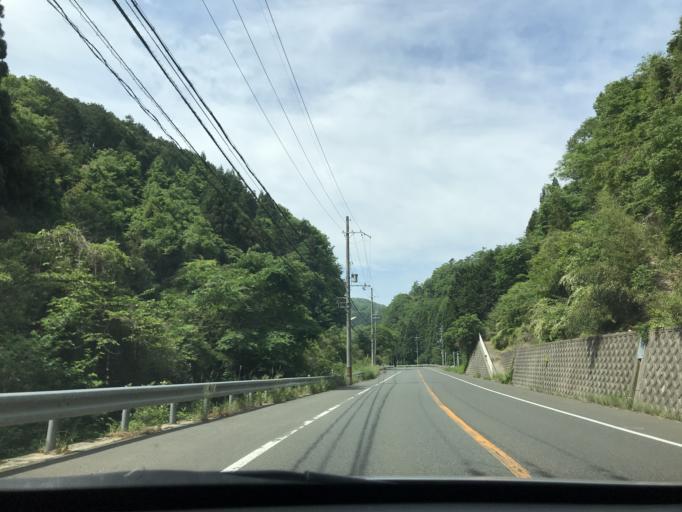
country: JP
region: Kyoto
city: Miyazu
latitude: 35.6614
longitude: 135.0099
